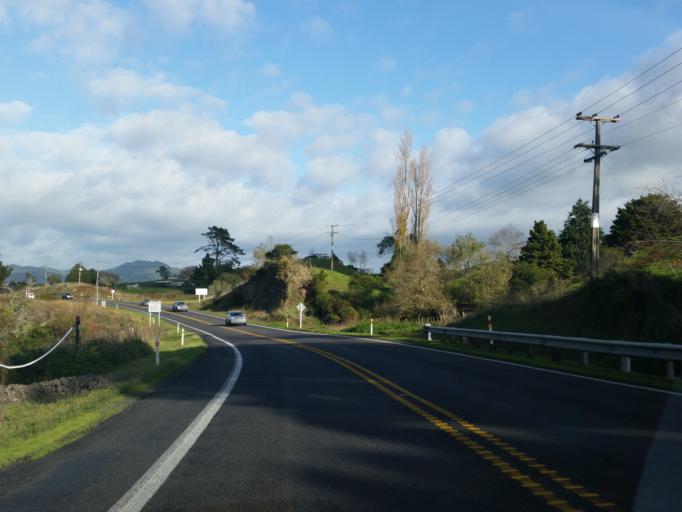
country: NZ
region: Waikato
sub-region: Hauraki District
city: Waihi
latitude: -37.4018
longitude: 175.8146
